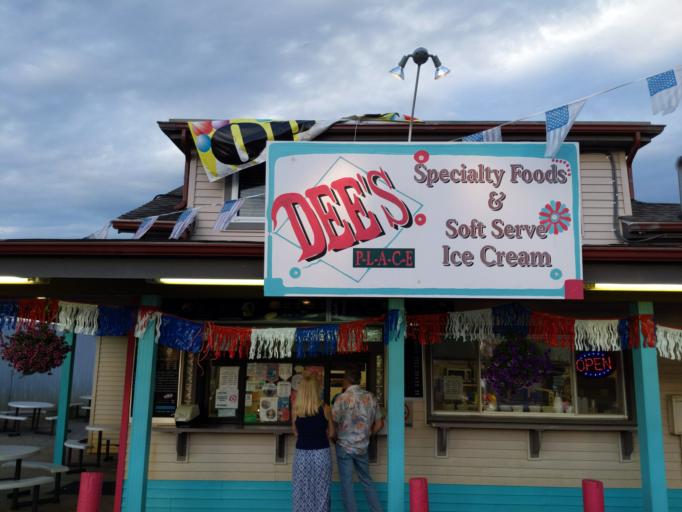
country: US
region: Michigan
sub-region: Livingston County
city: Whitmore Lake
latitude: 42.4273
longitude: -83.7645
